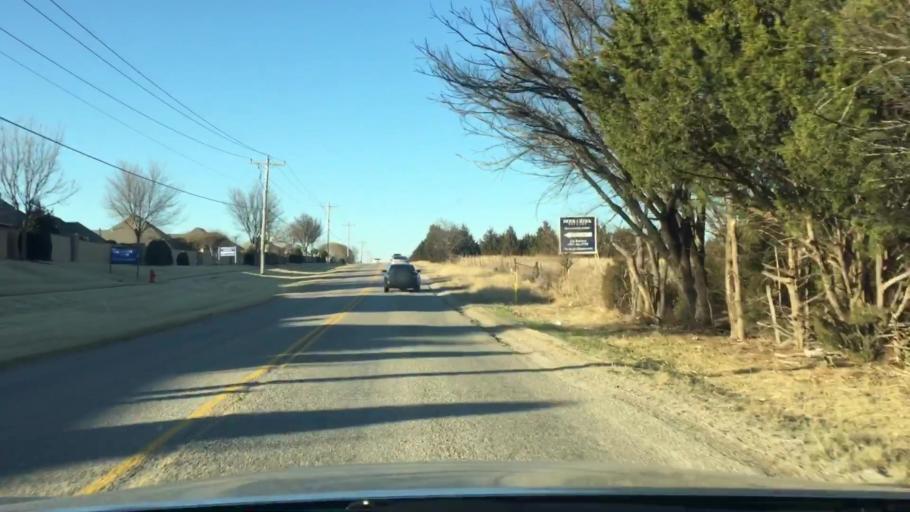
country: US
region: Oklahoma
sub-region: Oklahoma County
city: The Village
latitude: 35.6268
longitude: -97.6208
